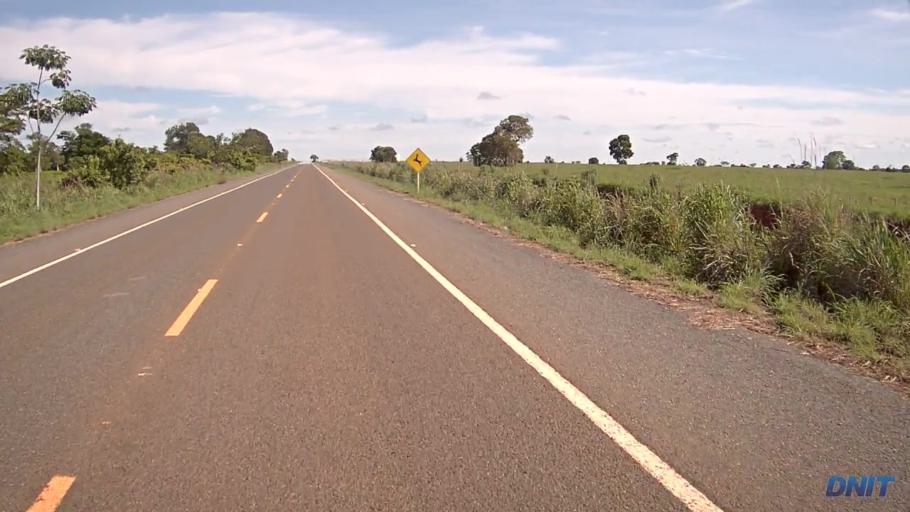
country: BR
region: Goias
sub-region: Sao Miguel Do Araguaia
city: Sao Miguel do Araguaia
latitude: -13.4443
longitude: -50.1225
